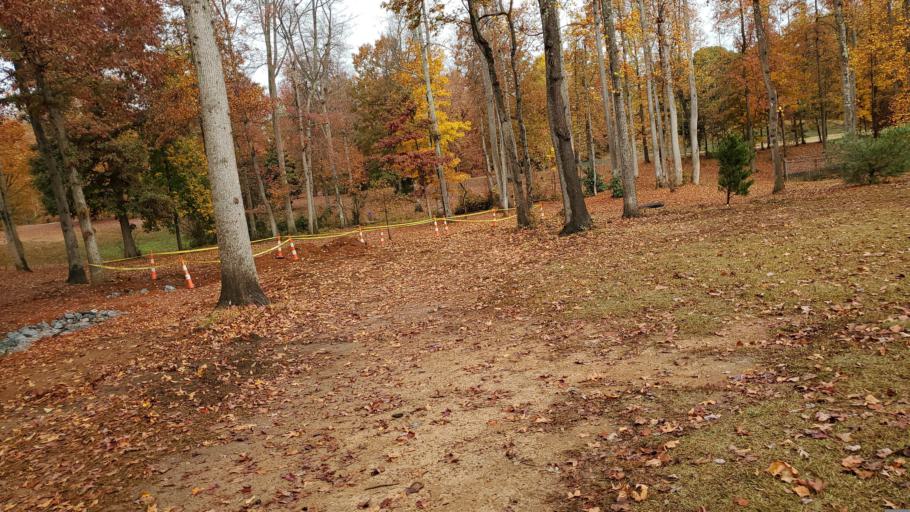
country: US
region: South Carolina
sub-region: Greenville County
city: Greer
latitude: 34.9292
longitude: -82.2410
